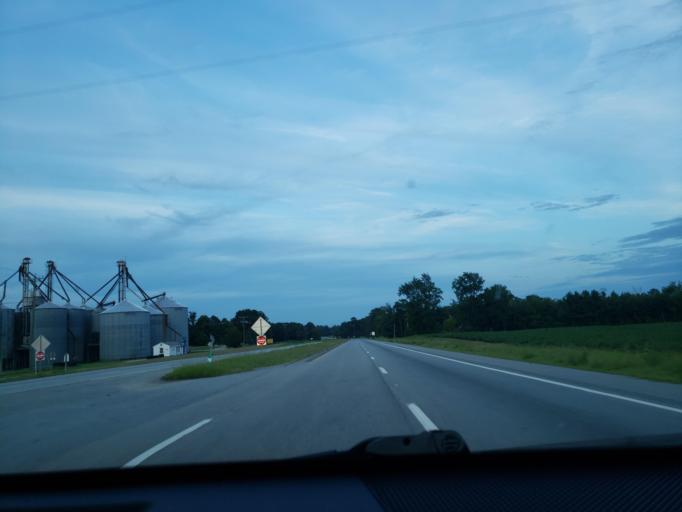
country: US
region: Virginia
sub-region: Southampton County
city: Courtland
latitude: 36.7057
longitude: -77.2012
